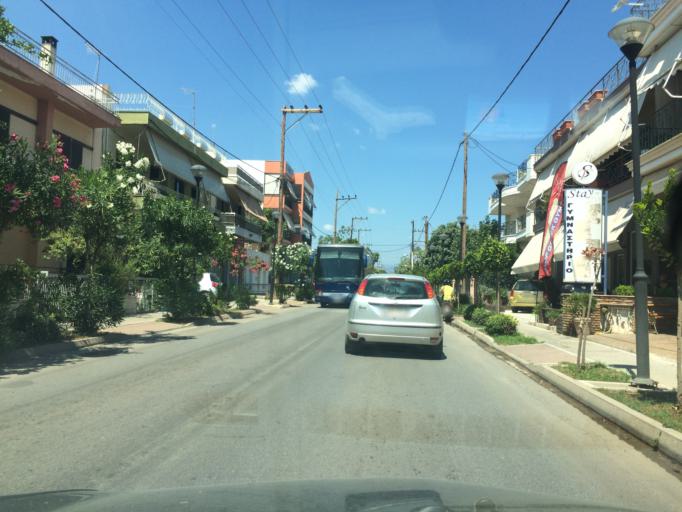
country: GR
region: Central Greece
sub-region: Nomos Evvoias
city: Nea Artaki
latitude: 38.5163
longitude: 23.6373
